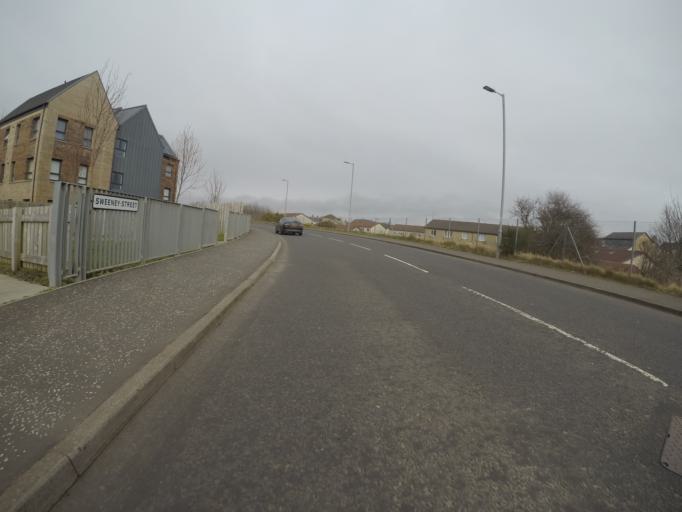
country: GB
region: Scotland
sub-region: North Ayrshire
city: Ardrossan
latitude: 55.6456
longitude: -4.8120
